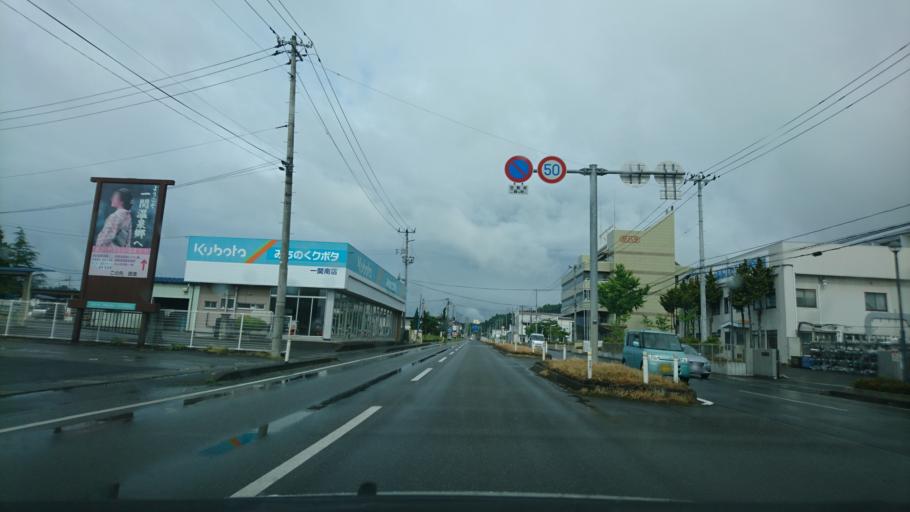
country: JP
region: Iwate
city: Ichinoseki
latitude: 38.9403
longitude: 141.0896
